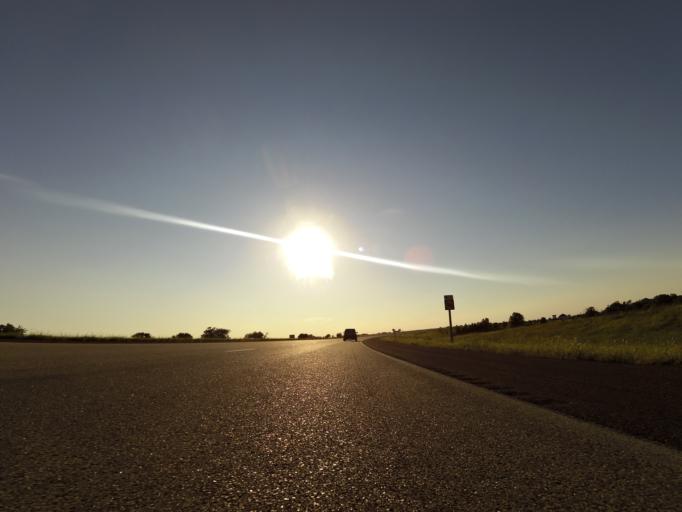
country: US
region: Kansas
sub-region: Reno County
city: Haven
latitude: 37.9368
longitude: -97.8736
